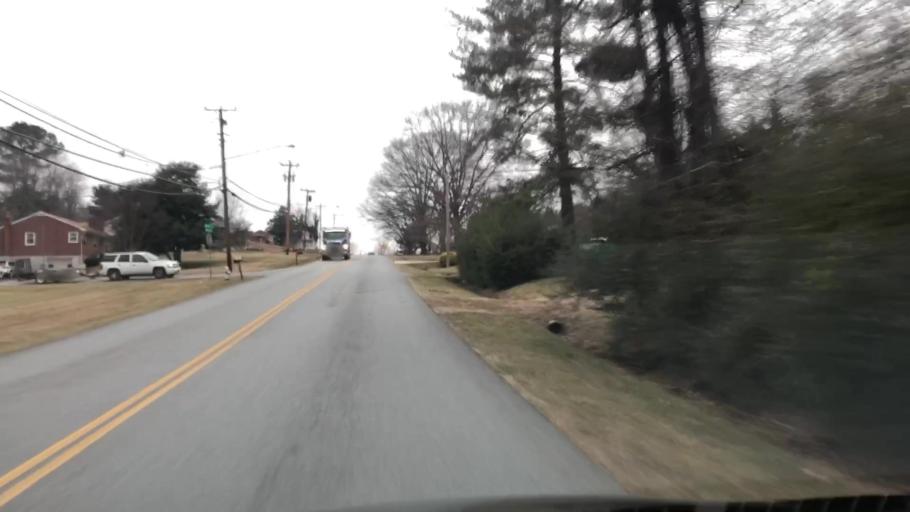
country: US
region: Virginia
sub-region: City of Lynchburg
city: West Lynchburg
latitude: 37.3463
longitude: -79.1923
